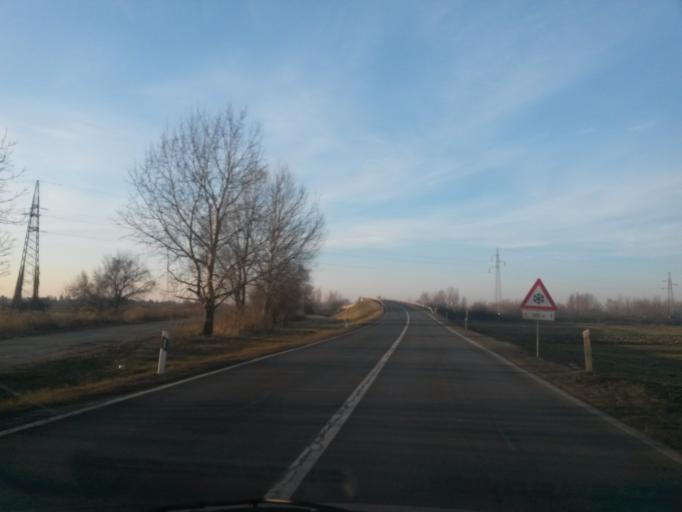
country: HR
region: Varazdinska
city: Jalzabet
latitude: 46.2928
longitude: 16.4967
